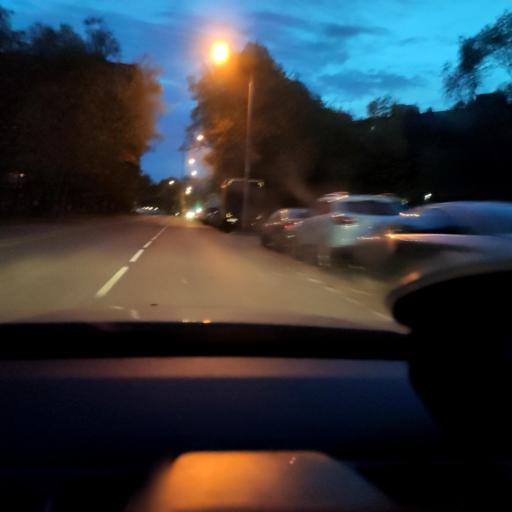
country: RU
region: Moscow
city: Yaroslavskiy
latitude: 55.8717
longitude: 37.7046
